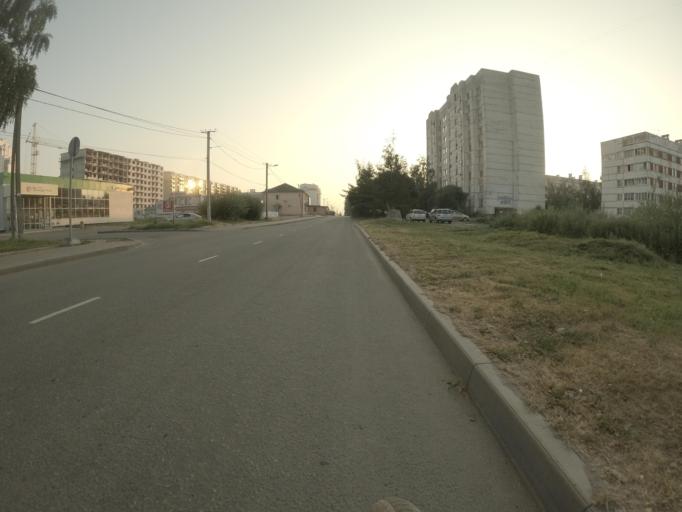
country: RU
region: St.-Petersburg
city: Pontonnyy
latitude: 59.7970
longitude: 30.6350
